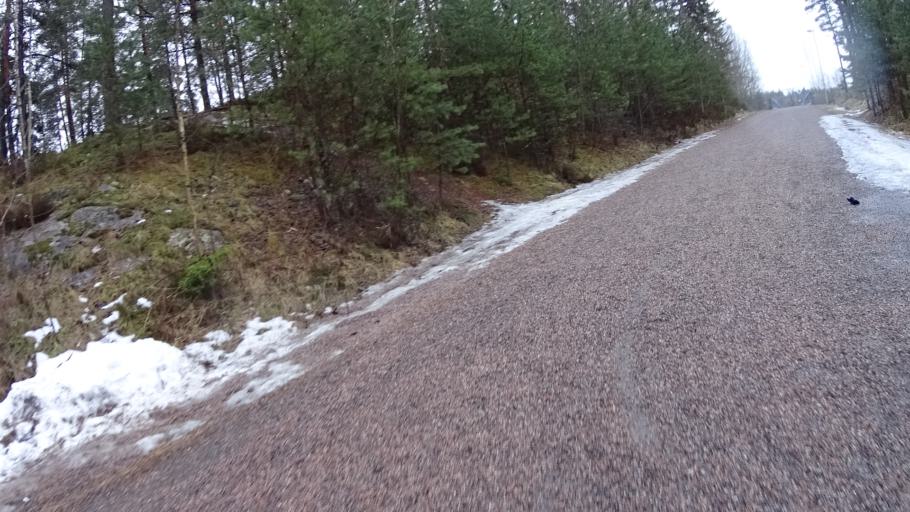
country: FI
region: Uusimaa
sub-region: Helsinki
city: Espoo
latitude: 60.2221
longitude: 24.6379
